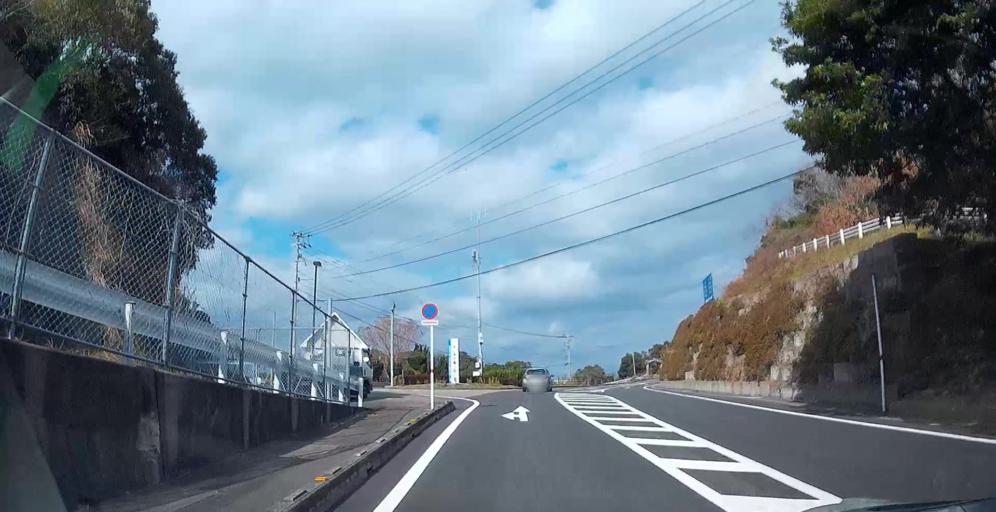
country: JP
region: Kumamoto
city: Minamata
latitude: 32.3221
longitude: 130.4712
